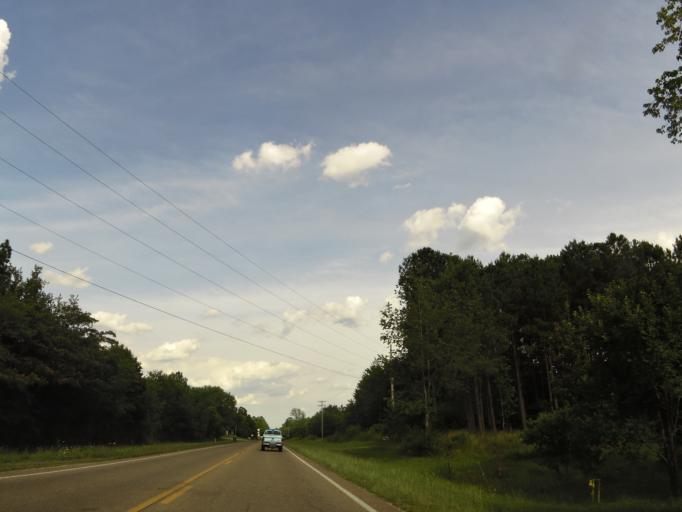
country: US
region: Tennessee
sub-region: Carroll County
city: Bruceton
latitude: 36.0375
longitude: -88.2972
